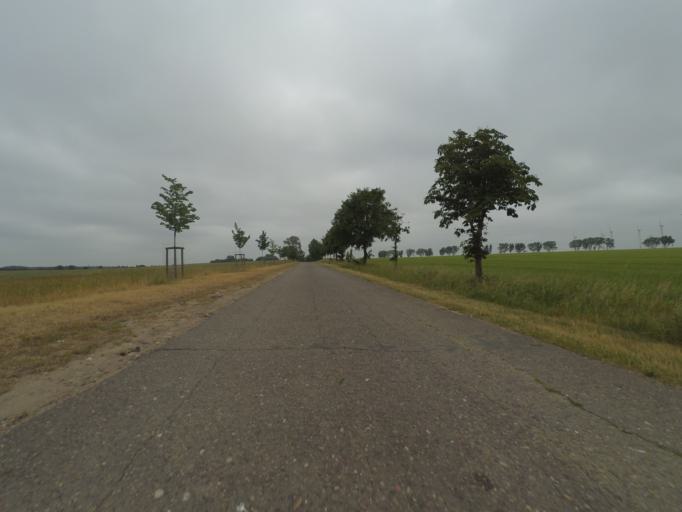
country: DE
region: Mecklenburg-Vorpommern
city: Plau am See
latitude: 53.4884
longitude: 12.2216
